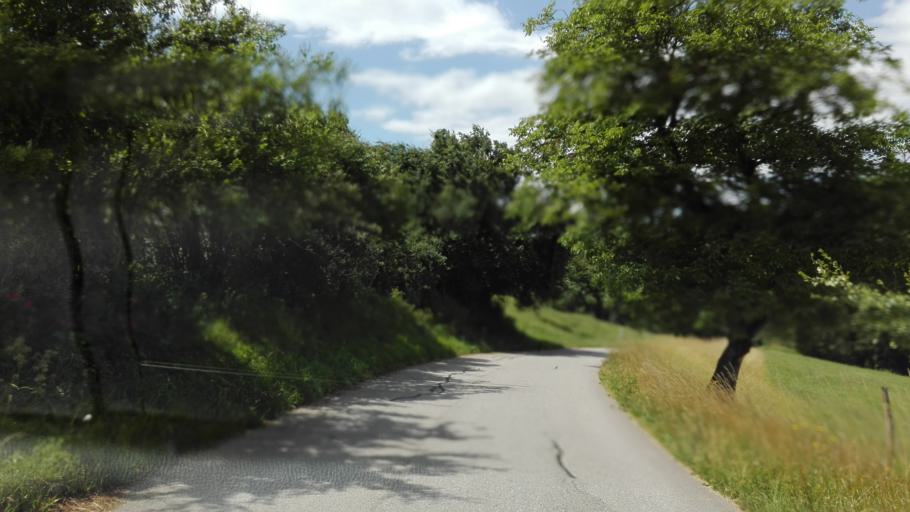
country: AT
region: Upper Austria
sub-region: Politischer Bezirk Perg
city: Bad Kreuzen
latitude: 48.2305
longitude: 14.7336
